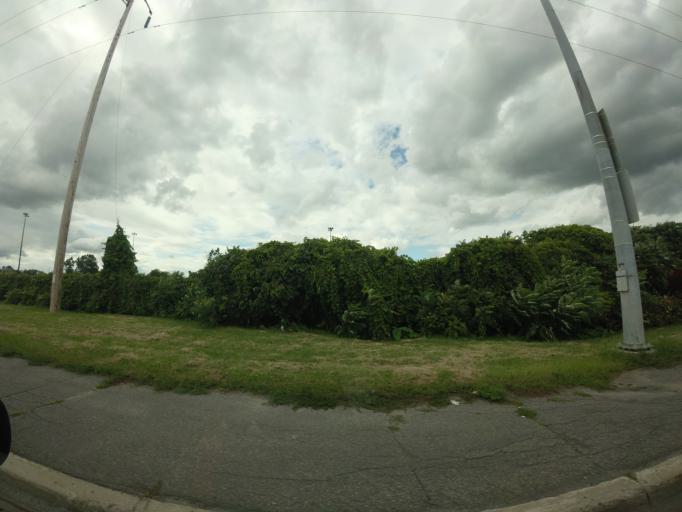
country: CA
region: Quebec
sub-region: Outaouais
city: Gatineau
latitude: 45.4804
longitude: -75.5154
